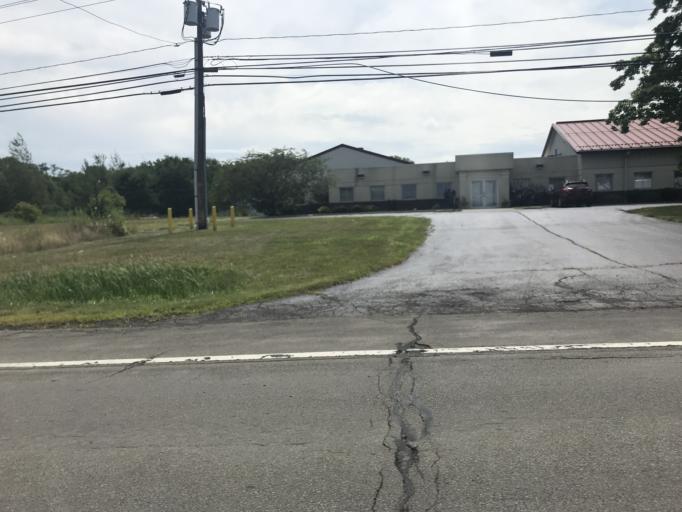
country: US
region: New York
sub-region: Chautauqua County
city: Dunkirk
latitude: 42.5042
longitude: -79.2970
